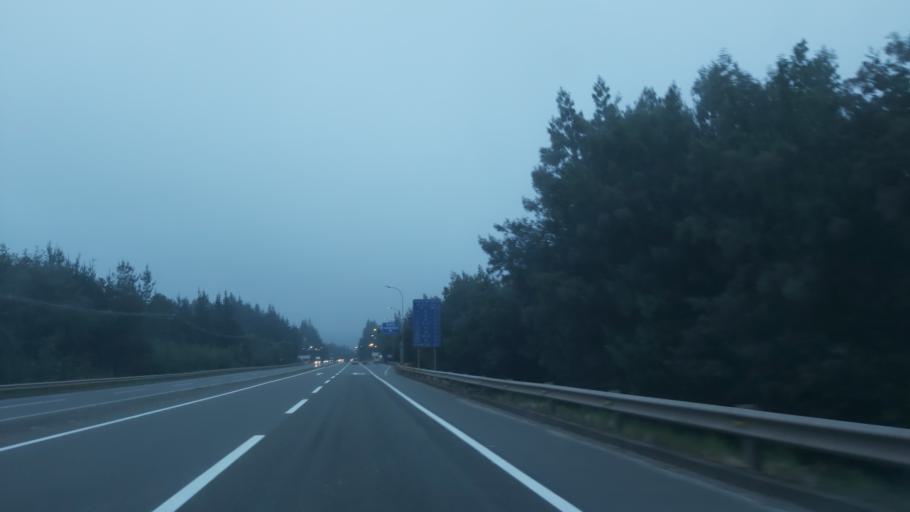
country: CL
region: Biobio
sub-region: Provincia de Concepcion
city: Penco
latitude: -36.7336
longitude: -72.8845
